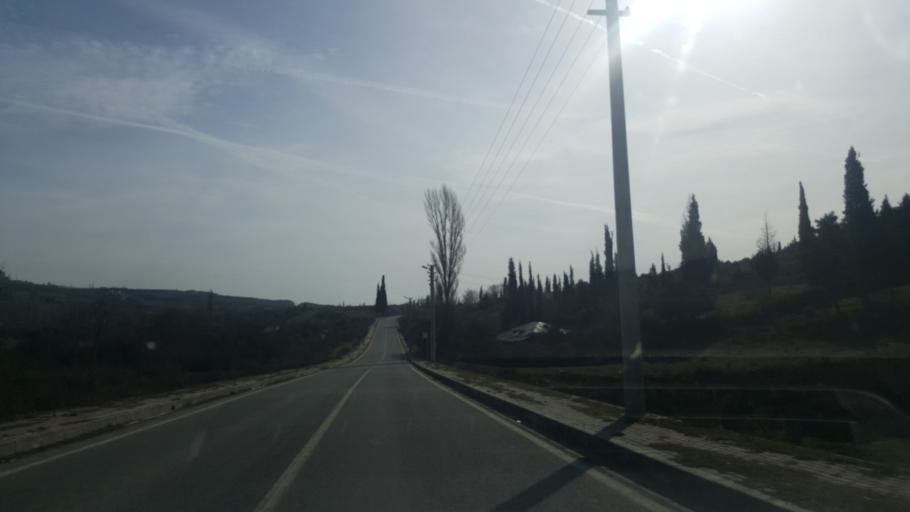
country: TR
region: Kocaeli
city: Tavsancil
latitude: 40.7891
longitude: 29.5671
